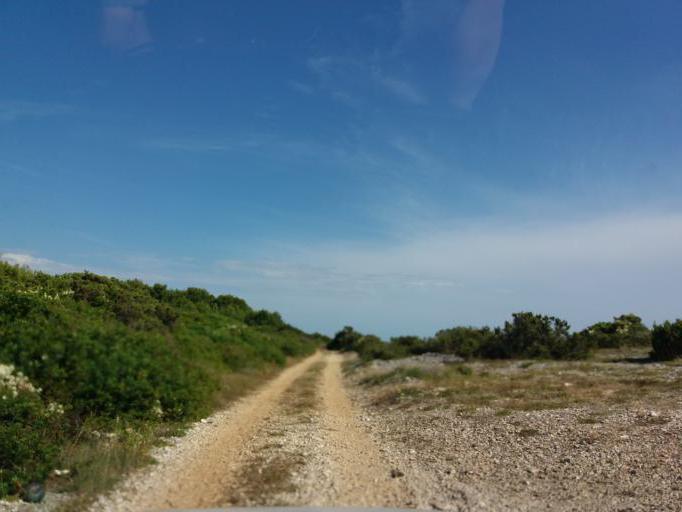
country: HR
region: Zadarska
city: Ugljan
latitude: 44.1296
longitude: 14.8650
